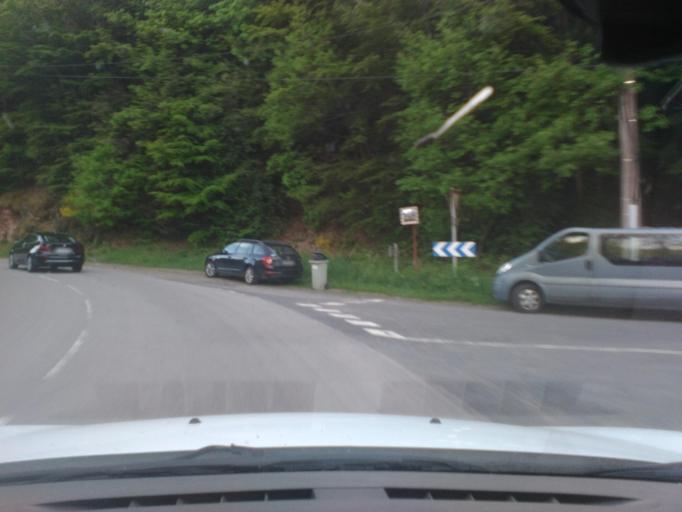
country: FR
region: Lorraine
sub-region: Departement des Vosges
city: Bruyeres
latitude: 48.2467
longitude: 6.7291
